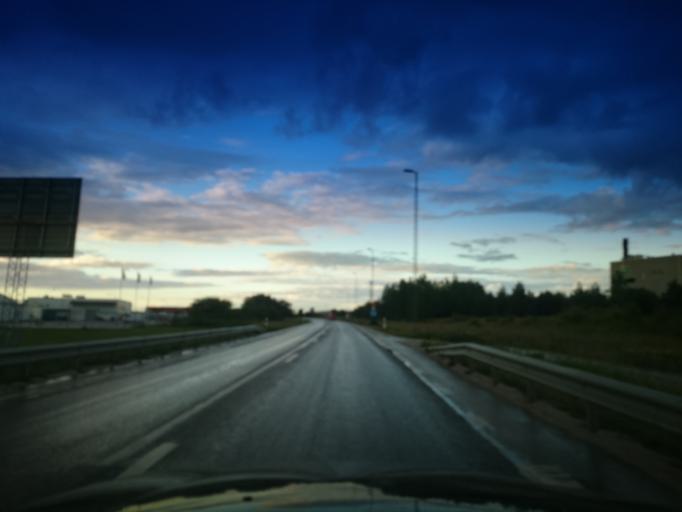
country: SE
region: Gotland
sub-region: Gotland
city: Visby
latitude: 57.6332
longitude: 18.3289
